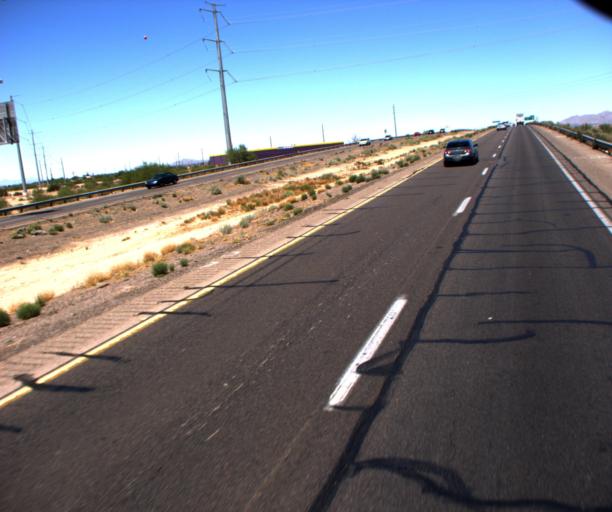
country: US
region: Arizona
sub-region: Pinal County
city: Arizona City
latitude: 32.8296
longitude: -111.6852
